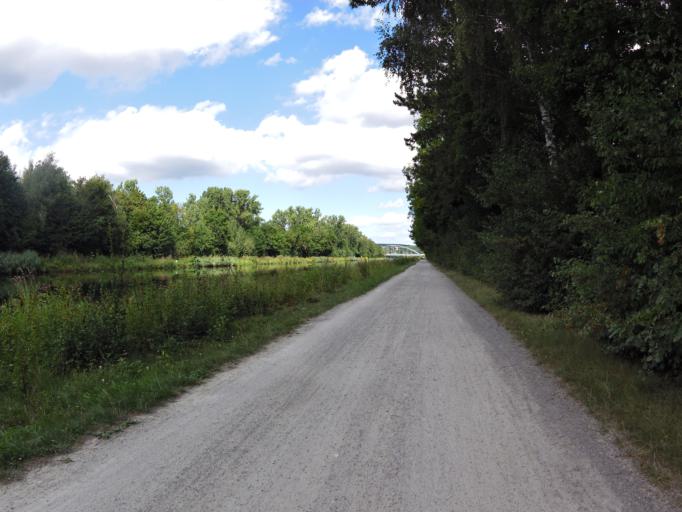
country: DE
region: Bavaria
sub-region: Regierungsbezirk Unterfranken
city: Volkach
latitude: 49.8557
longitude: 10.2249
